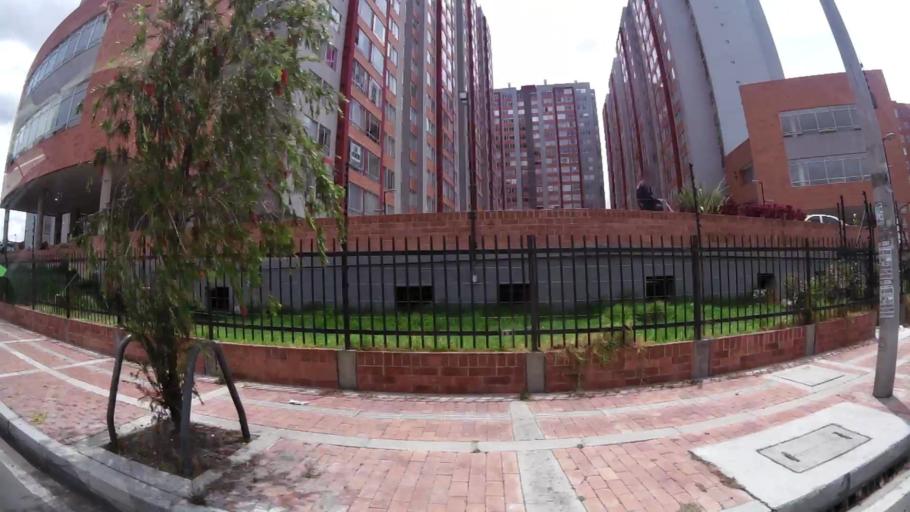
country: CO
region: Bogota D.C.
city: Bogota
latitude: 4.6374
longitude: -74.1529
